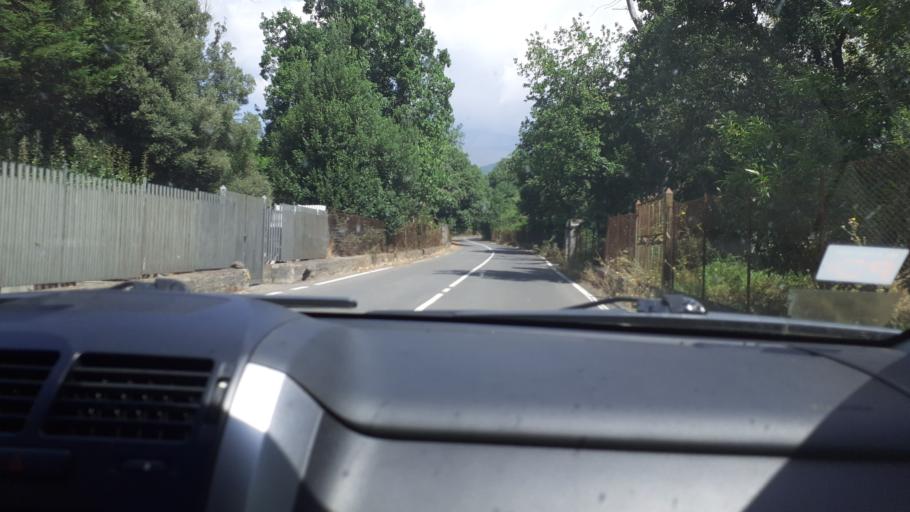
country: IT
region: Sicily
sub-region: Catania
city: Nicolosi
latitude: 37.6430
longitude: 15.0200
